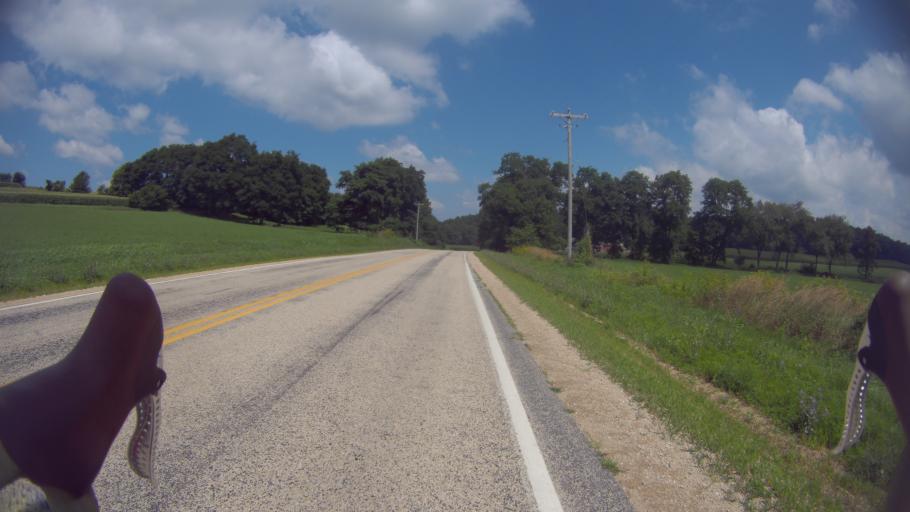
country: US
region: Wisconsin
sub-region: Columbia County
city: Lodi
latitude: 43.2450
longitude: -89.6052
